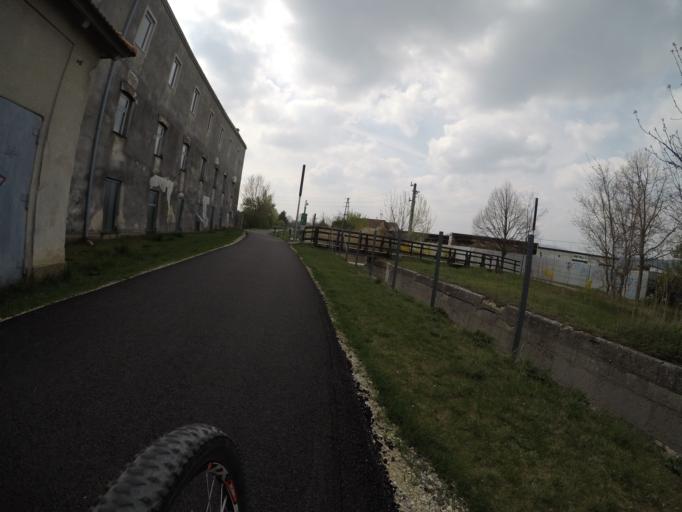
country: AT
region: Lower Austria
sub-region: Politischer Bezirk Baden
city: Pfaffstatten
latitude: 48.0113
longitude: 16.2672
